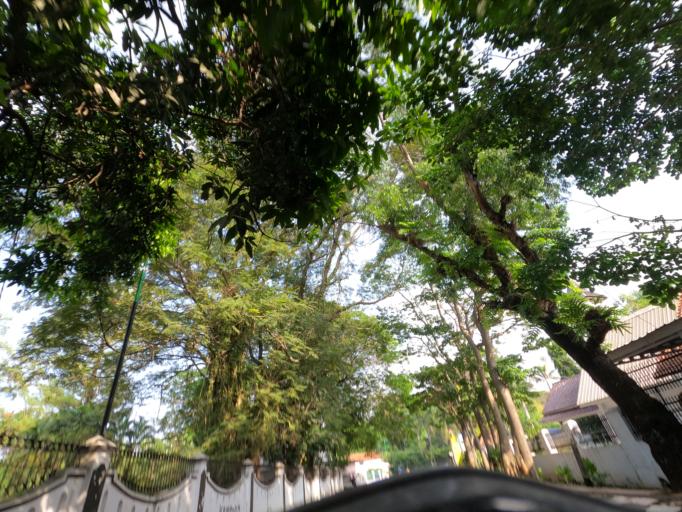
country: ID
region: West Java
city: Lembang
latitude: -6.5741
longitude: 107.7634
